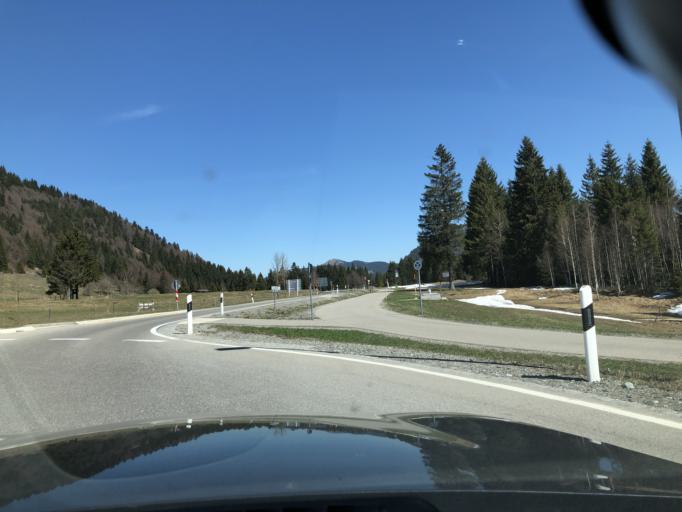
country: AT
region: Tyrol
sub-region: Politischer Bezirk Reutte
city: Schattwald
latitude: 47.5173
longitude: 10.4087
